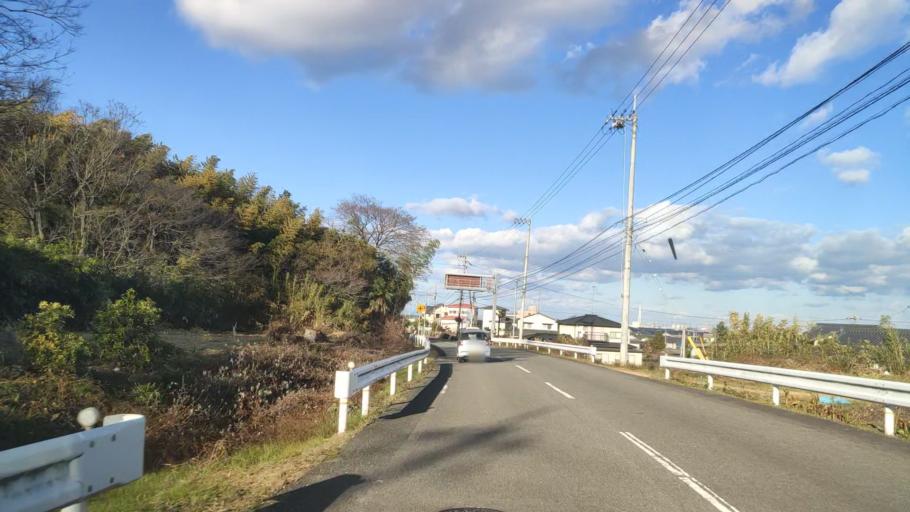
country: JP
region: Ehime
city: Saijo
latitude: 33.8899
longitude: 133.1310
